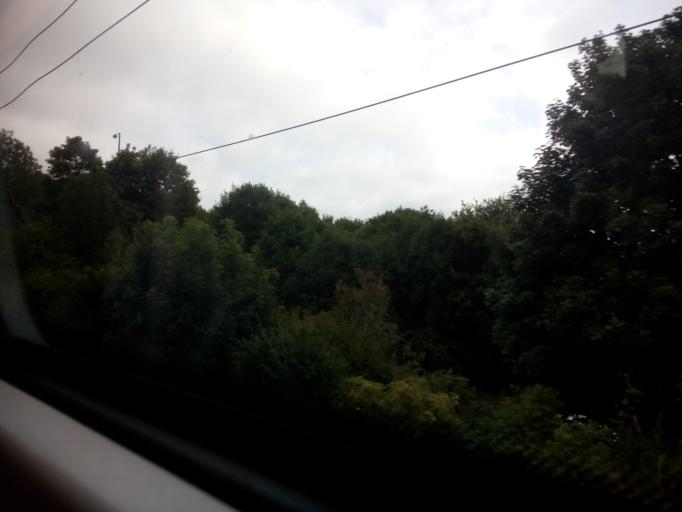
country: GB
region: England
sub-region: County Durham
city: Chester-le-Street
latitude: 54.8548
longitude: -1.5779
